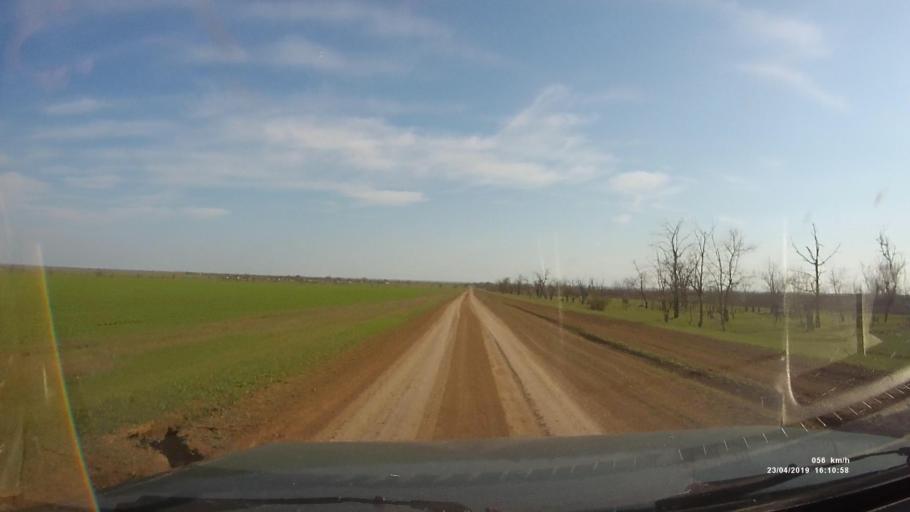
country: RU
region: Rostov
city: Remontnoye
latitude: 46.4780
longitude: 43.1231
